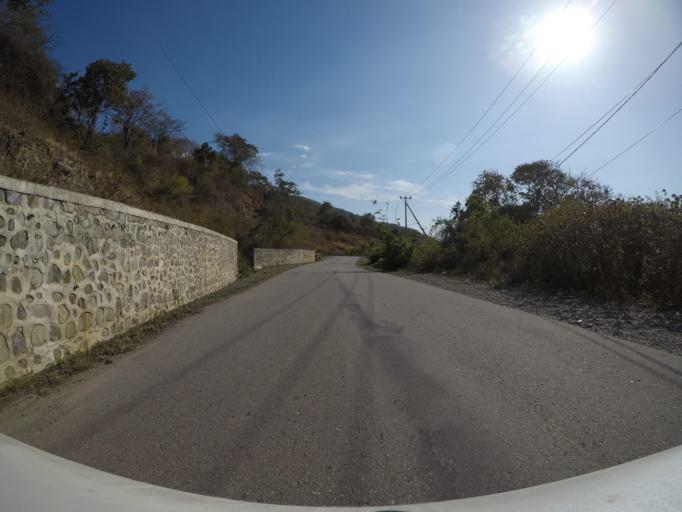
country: TL
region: Liquica
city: Maubara
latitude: -8.6349
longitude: 125.1439
